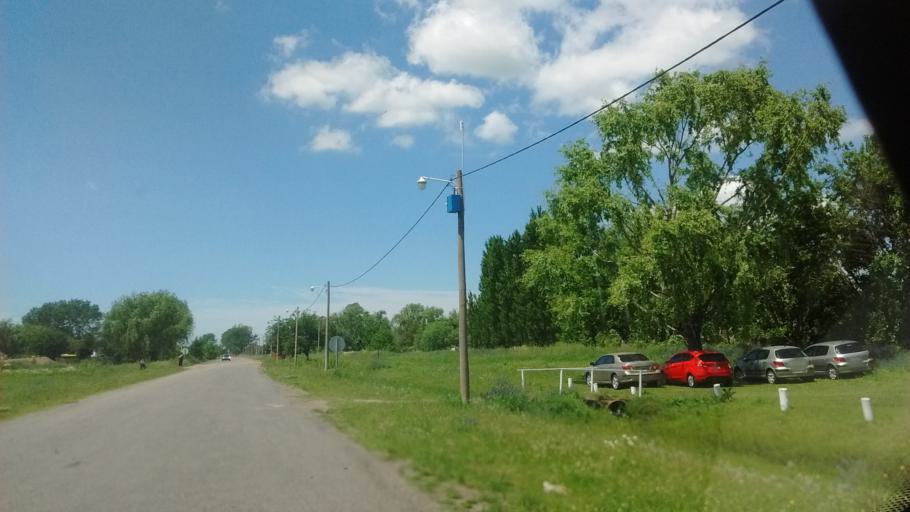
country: AR
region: Santa Fe
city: Funes
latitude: -32.8474
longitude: -60.7969
